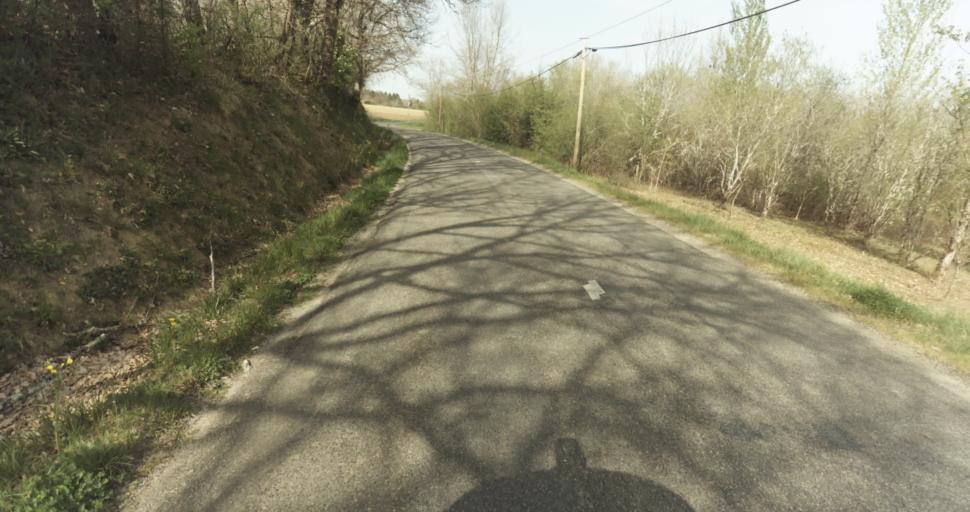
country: FR
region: Midi-Pyrenees
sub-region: Departement du Tarn-et-Garonne
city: Lafrancaise
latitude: 44.1356
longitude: 1.1715
